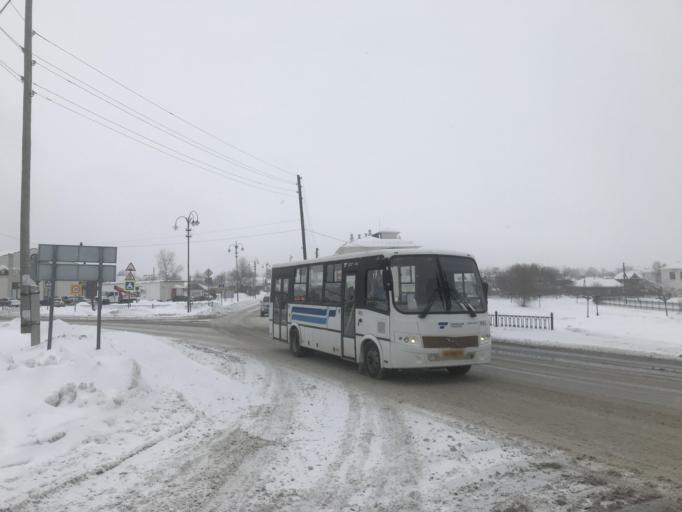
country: RU
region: Tjumen
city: Tobol'sk
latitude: 58.1963
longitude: 68.2552
